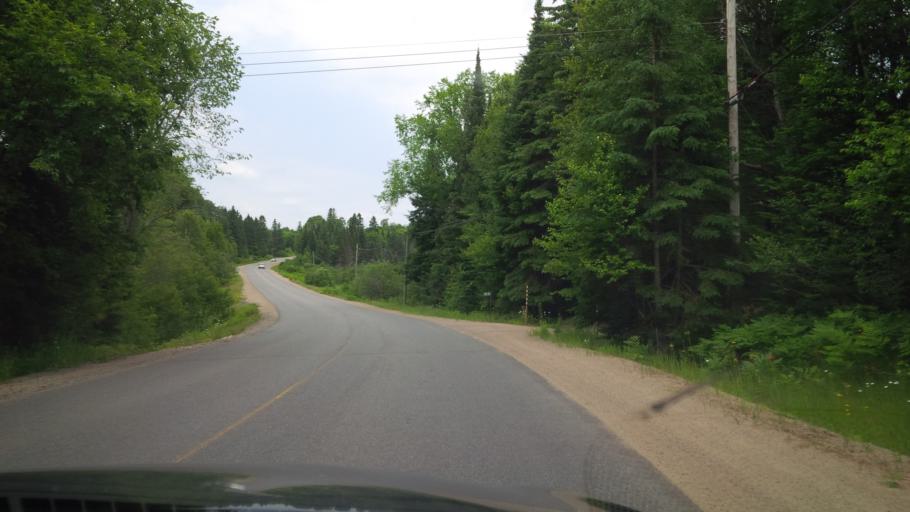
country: CA
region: Ontario
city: Huntsville
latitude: 45.6040
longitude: -79.1769
